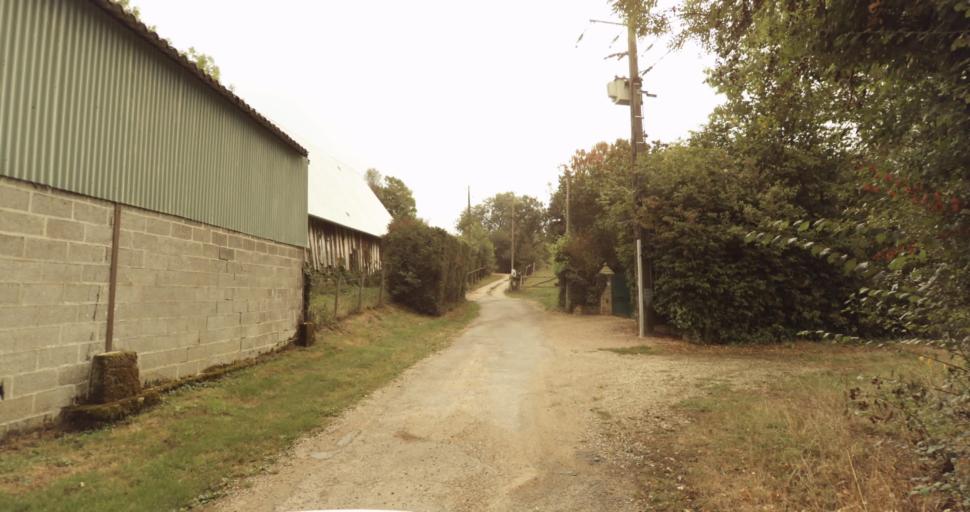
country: FR
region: Lower Normandy
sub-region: Departement de l'Orne
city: Trun
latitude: 48.9216
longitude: 0.0849
